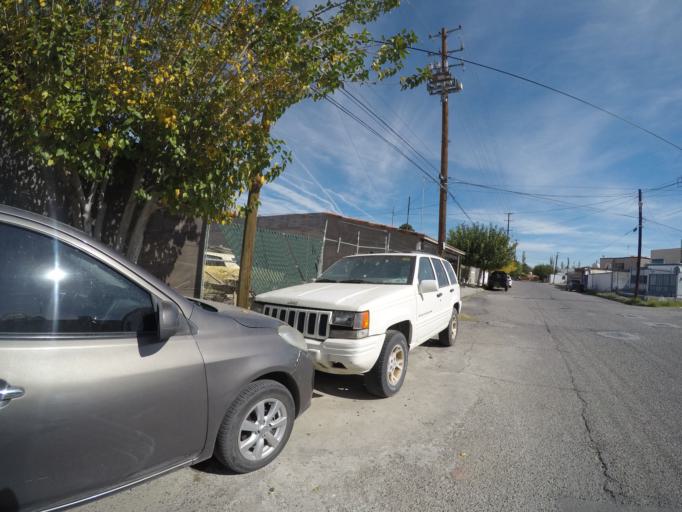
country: MX
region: Chihuahua
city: Ciudad Juarez
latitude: 31.7348
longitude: -106.4373
